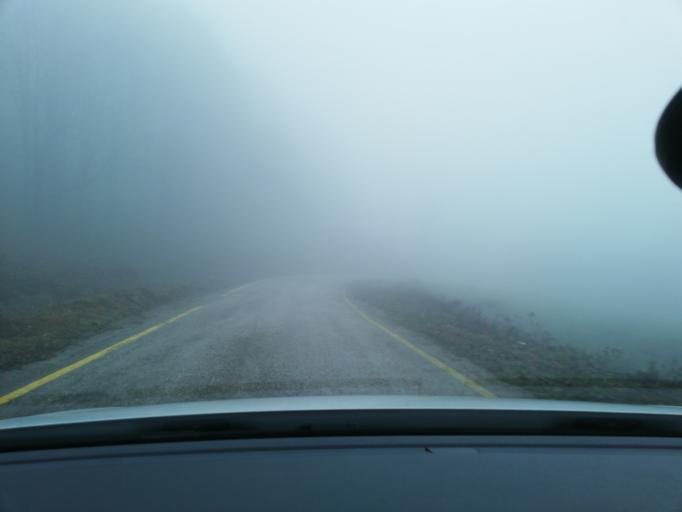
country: TR
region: Duzce
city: Kaynasli
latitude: 40.7525
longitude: 31.3774
